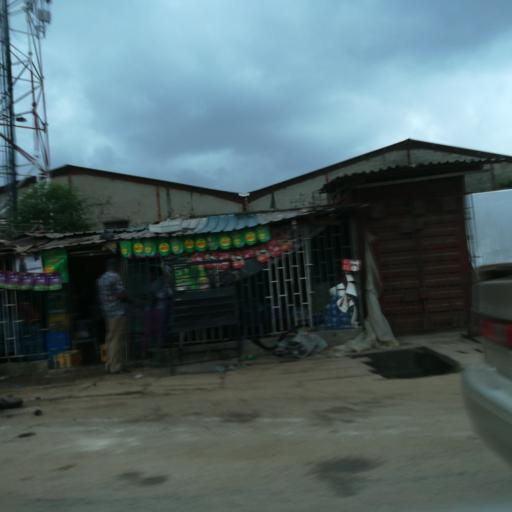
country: NG
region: Lagos
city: Agege
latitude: 6.6122
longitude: 3.3000
